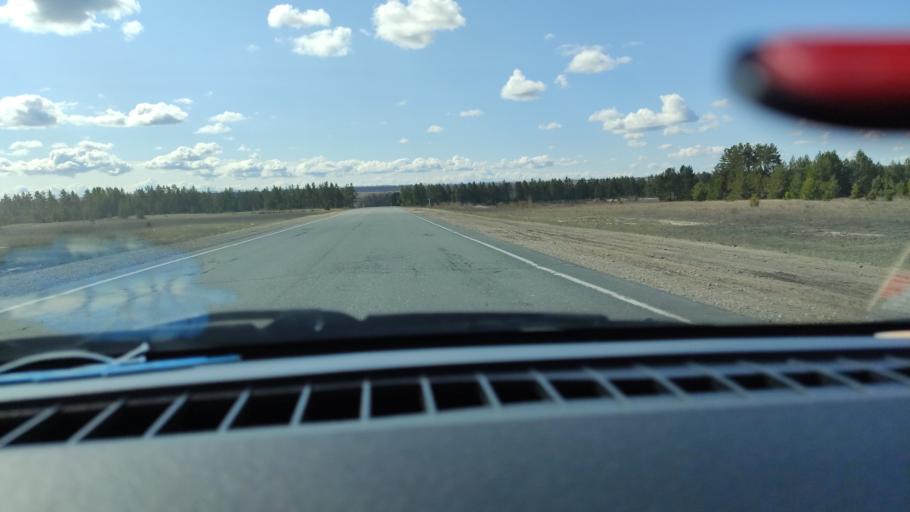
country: RU
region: Samara
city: Varlamovo
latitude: 53.1473
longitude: 48.2843
